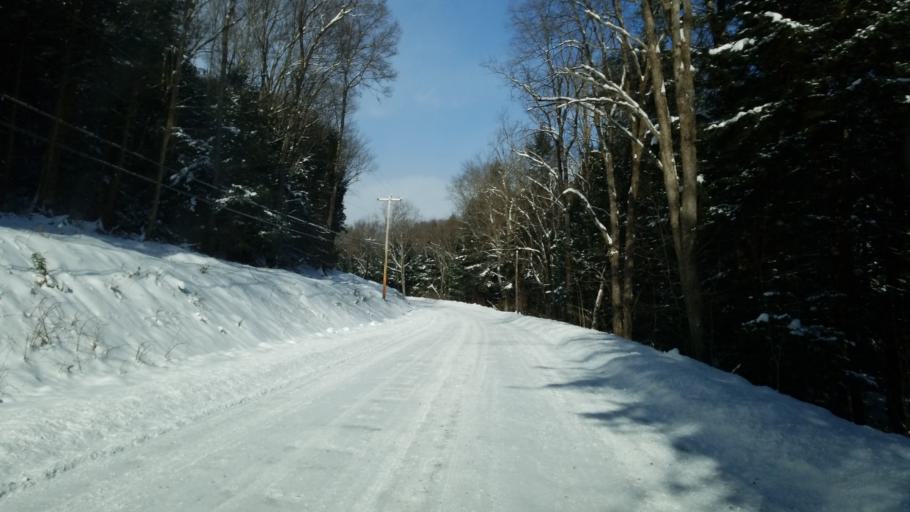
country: US
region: Pennsylvania
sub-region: Clearfield County
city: Clearfield
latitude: 41.0499
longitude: -78.4648
